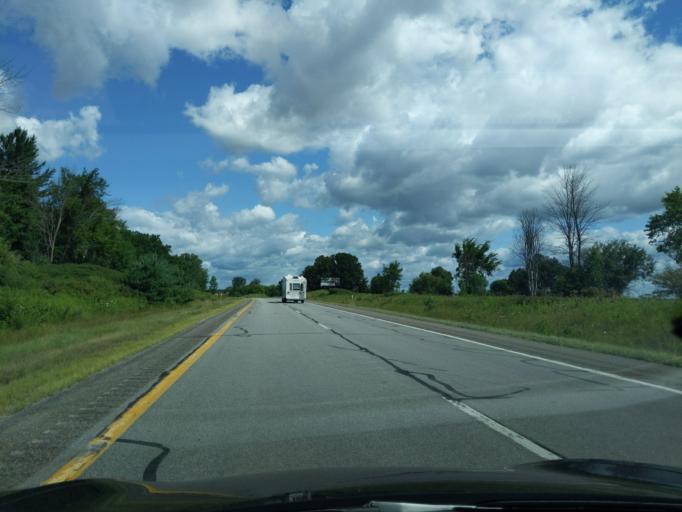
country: US
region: Michigan
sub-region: Clare County
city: Clare
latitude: 43.7509
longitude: -84.7574
